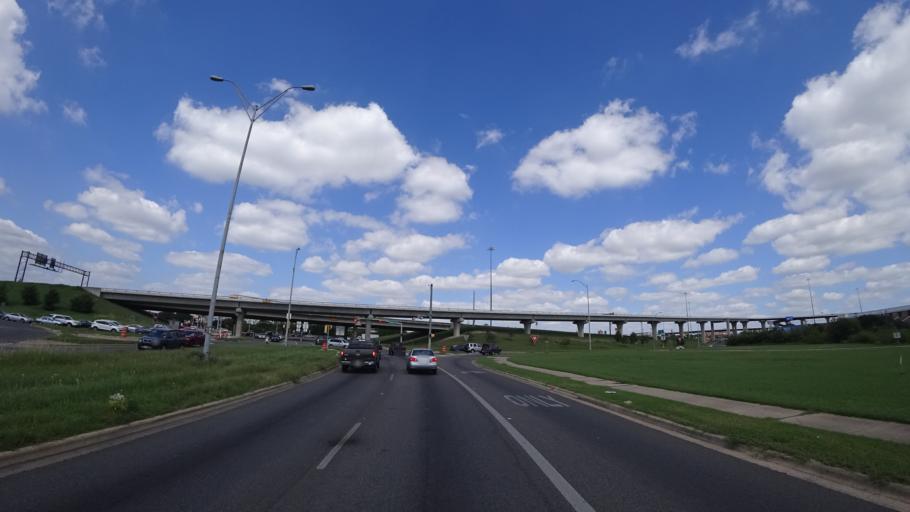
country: US
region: Texas
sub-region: Travis County
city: Austin
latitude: 30.3194
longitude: -97.7125
